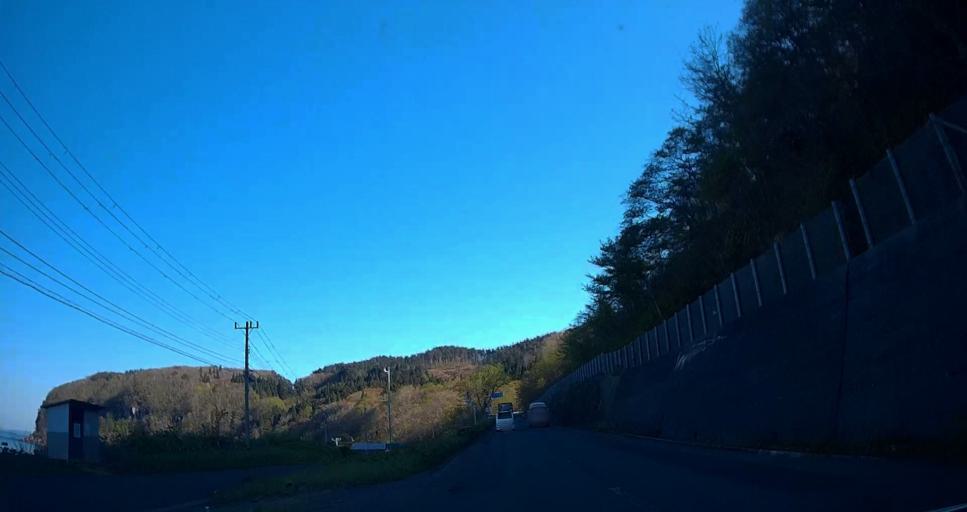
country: JP
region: Aomori
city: Mutsu
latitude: 41.4374
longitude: 141.1323
